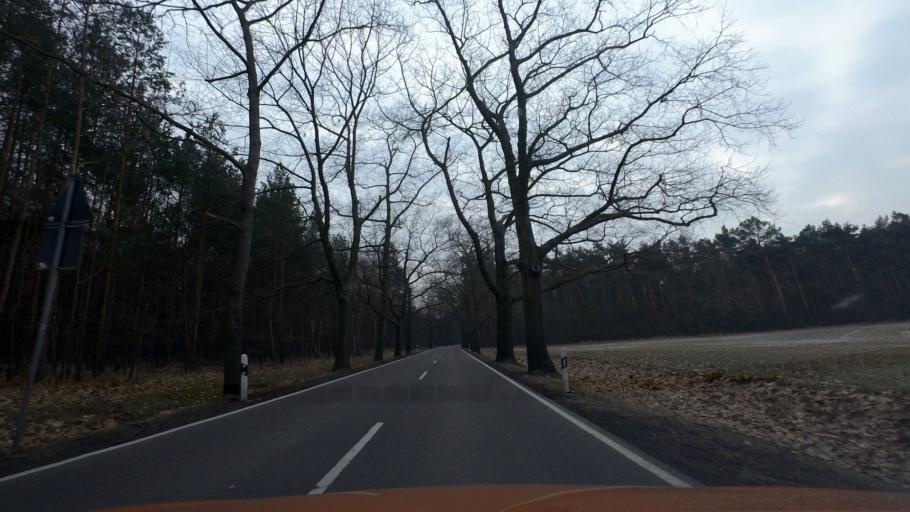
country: DE
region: Brandenburg
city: Ludwigsfelde
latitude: 52.2725
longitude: 13.2194
